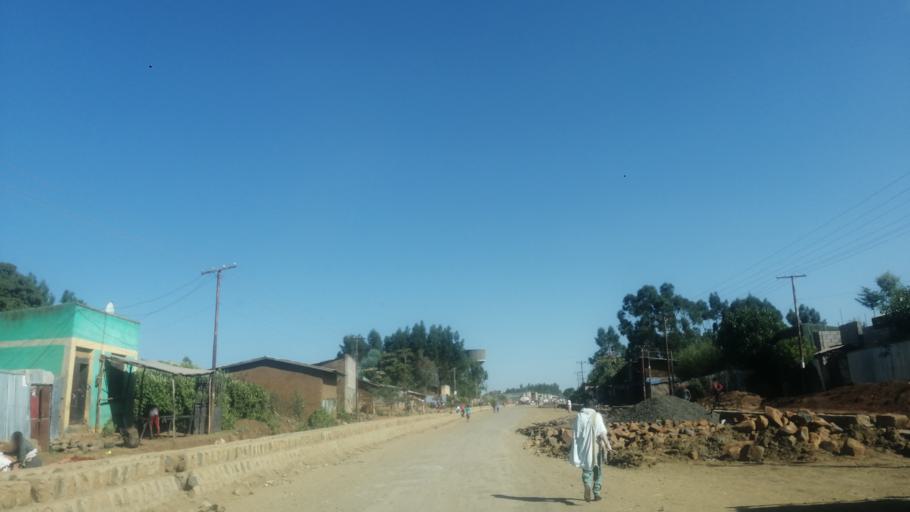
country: ET
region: Amhara
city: Addiet Canna
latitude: 11.0828
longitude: 37.8743
